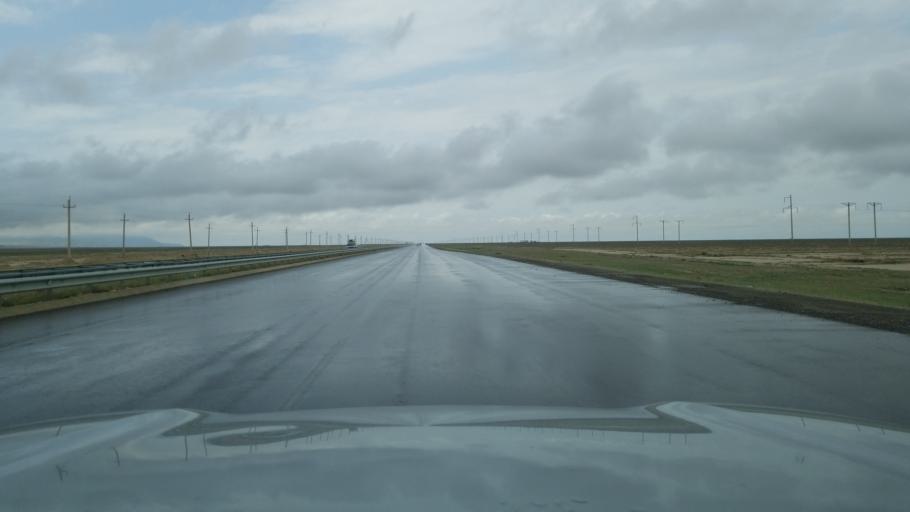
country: TM
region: Balkan
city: Gazanjyk
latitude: 39.1347
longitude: 55.8834
